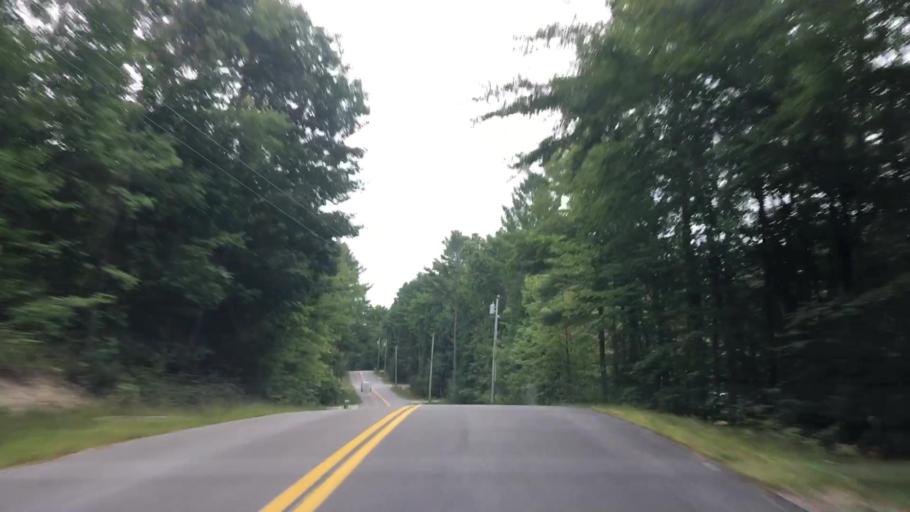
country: US
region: Maine
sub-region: Cumberland County
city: New Gloucester
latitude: 43.9118
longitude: -70.2409
